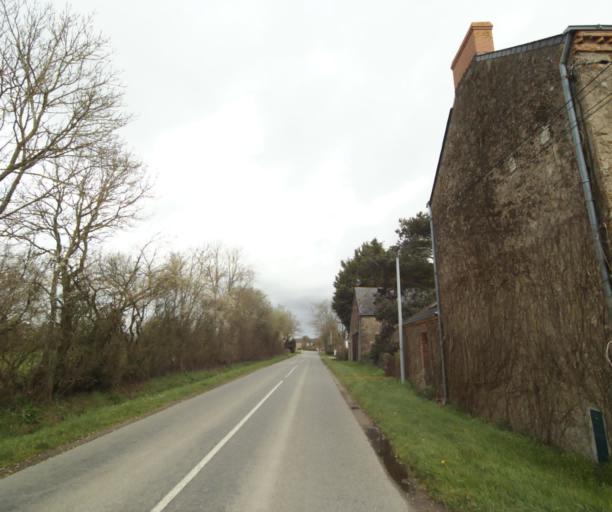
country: FR
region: Pays de la Loire
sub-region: Departement de la Loire-Atlantique
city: Bouvron
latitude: 47.4371
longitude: -1.8515
